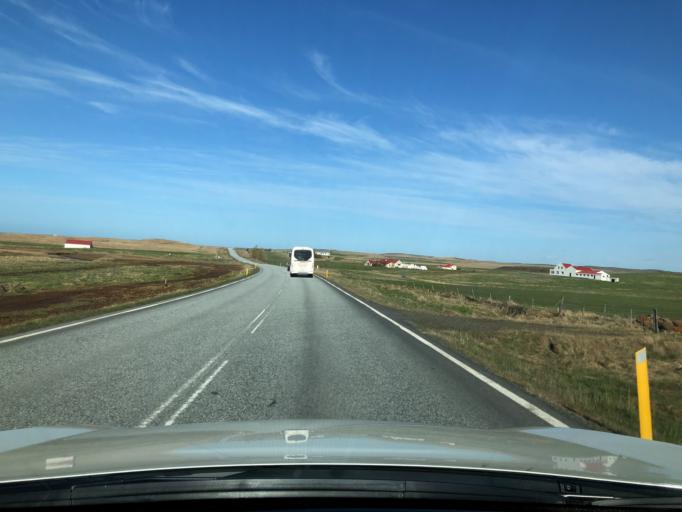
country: IS
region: West
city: Borgarnes
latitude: 64.3968
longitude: -21.8689
